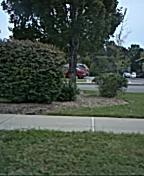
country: US
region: Kentucky
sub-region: Jefferson County
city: Hurstbourne
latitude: 38.2438
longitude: -85.5767
